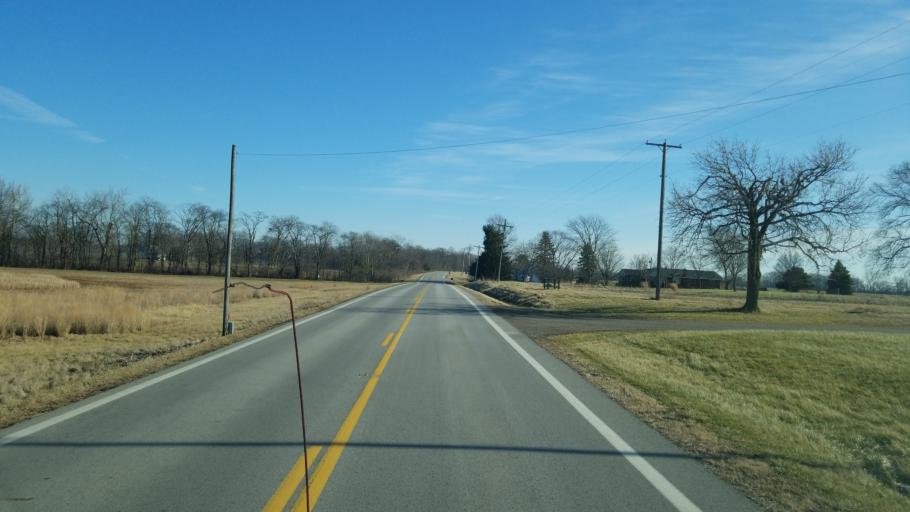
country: US
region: Ohio
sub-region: Henry County
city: Liberty Center
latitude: 41.4145
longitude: -83.9051
